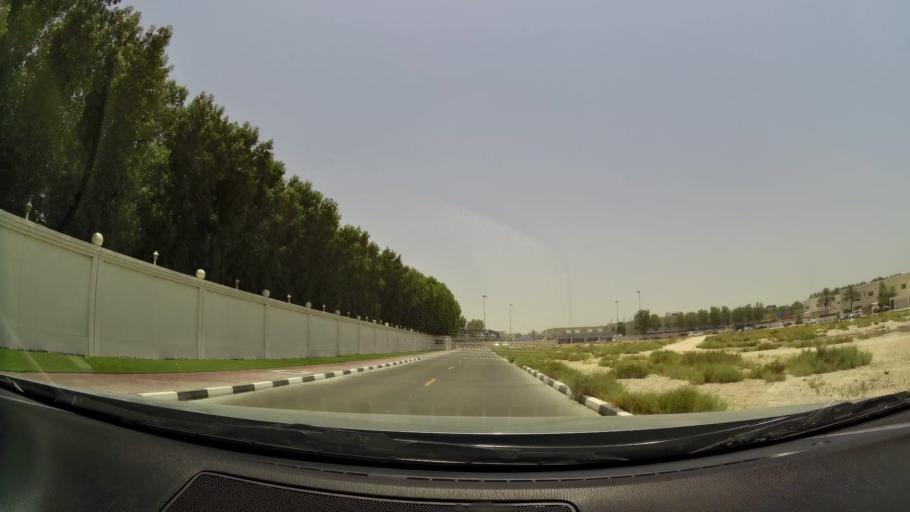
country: AE
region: Dubai
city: Dubai
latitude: 25.1773
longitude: 55.2405
